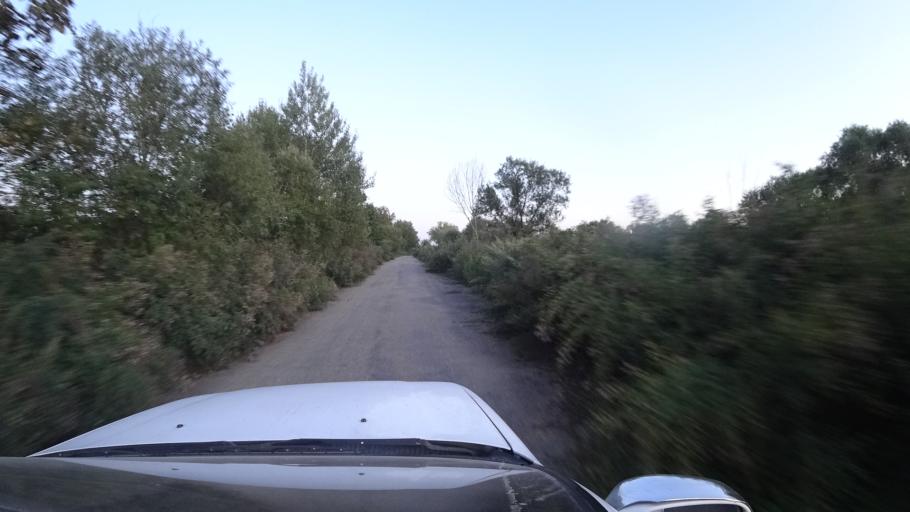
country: RU
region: Primorskiy
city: Dal'nerechensk
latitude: 45.9467
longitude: 133.7639
